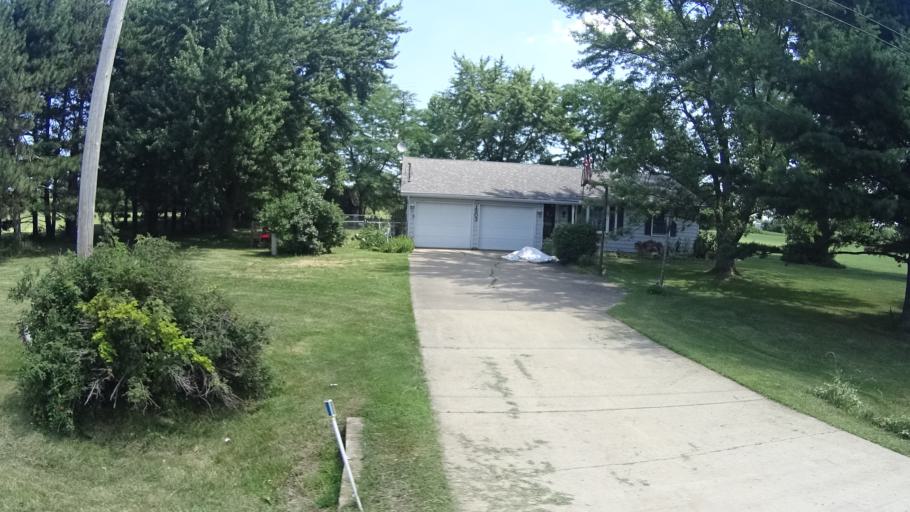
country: US
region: Ohio
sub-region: Erie County
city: Huron
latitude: 41.3999
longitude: -82.5931
